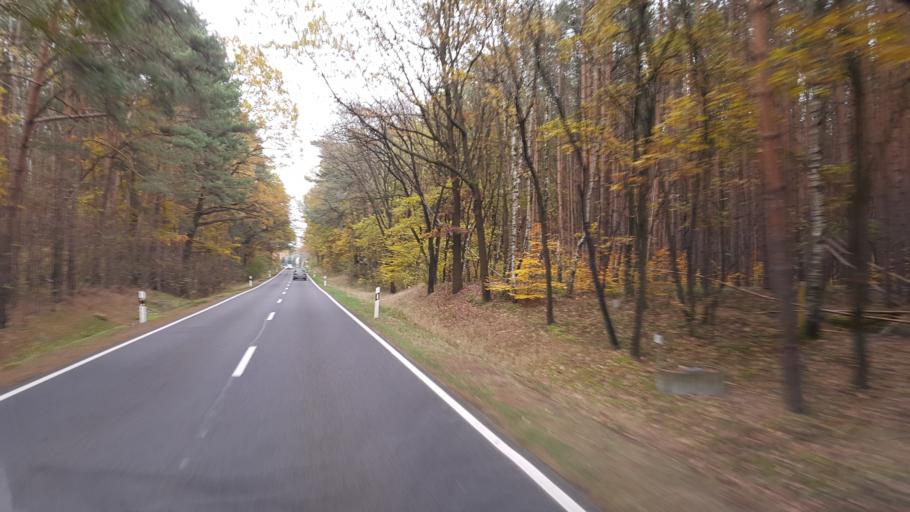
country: DE
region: Brandenburg
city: Crinitz
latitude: 51.7382
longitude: 13.7476
